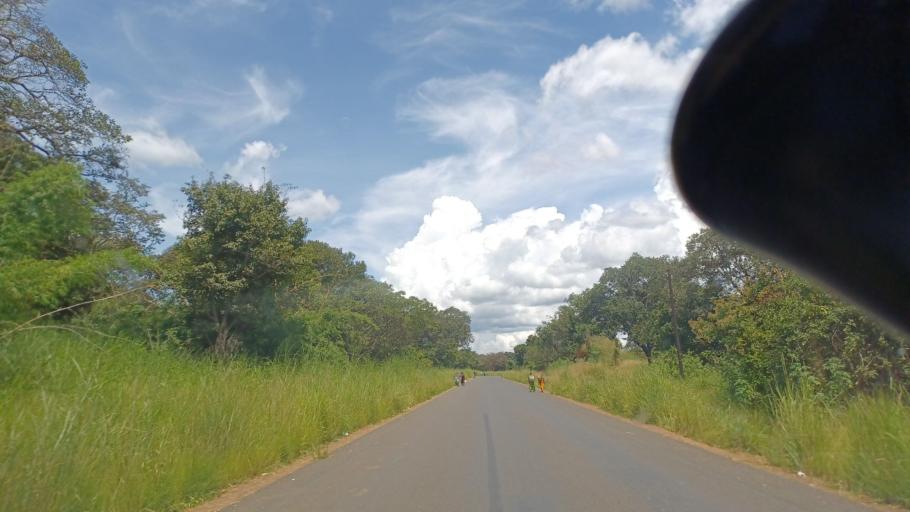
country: ZM
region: North-Western
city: Solwezi
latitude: -12.4024
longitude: 26.2397
